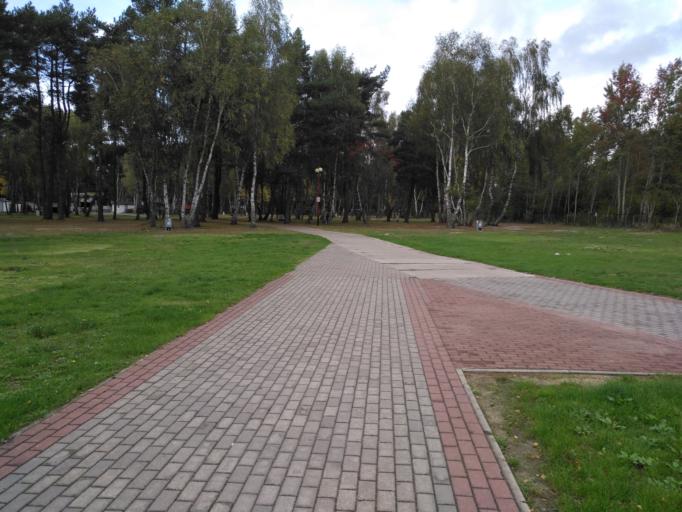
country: PL
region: West Pomeranian Voivodeship
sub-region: Powiat kolobrzeski
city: Grzybowo
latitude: 54.1604
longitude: 15.4261
